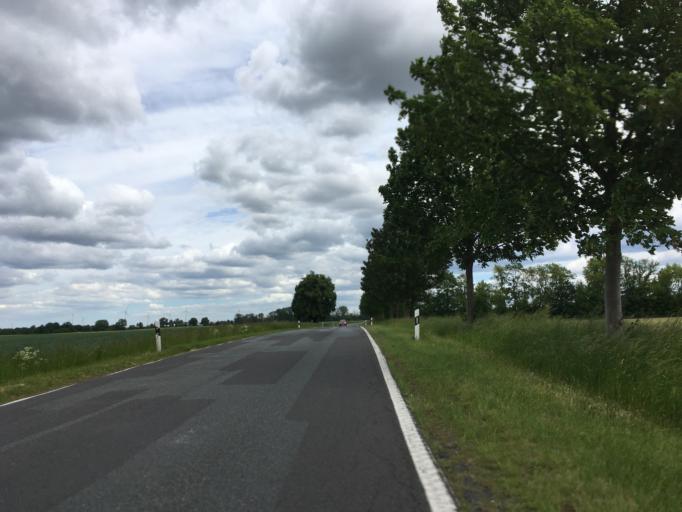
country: DE
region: Brandenburg
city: Werftpfuhl
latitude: 52.7354
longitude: 13.8183
